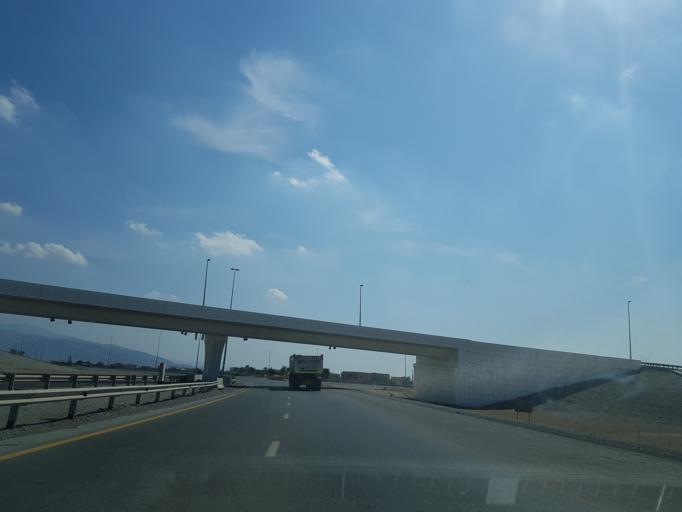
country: AE
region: Ra's al Khaymah
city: Ras al-Khaimah
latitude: 25.8340
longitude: 56.0153
